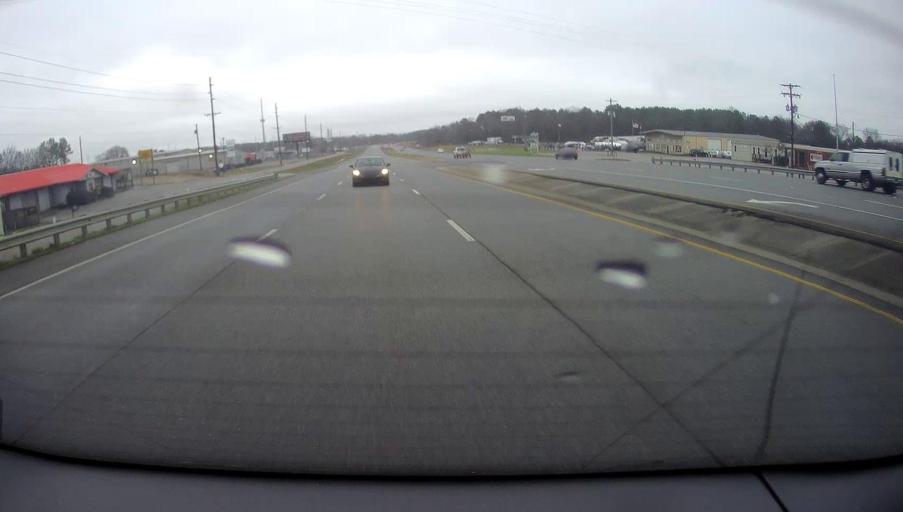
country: US
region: Alabama
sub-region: Morgan County
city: Decatur
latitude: 34.6111
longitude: -87.0313
